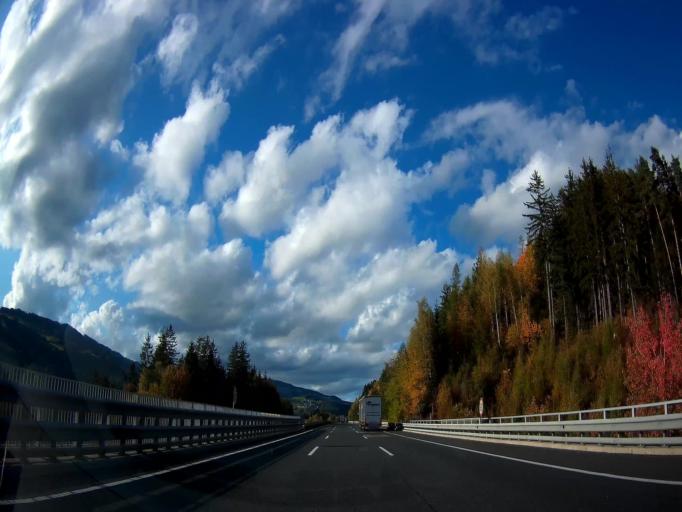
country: AT
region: Carinthia
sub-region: Politischer Bezirk Wolfsberg
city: Wolfsberg
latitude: 46.8885
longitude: 14.8262
